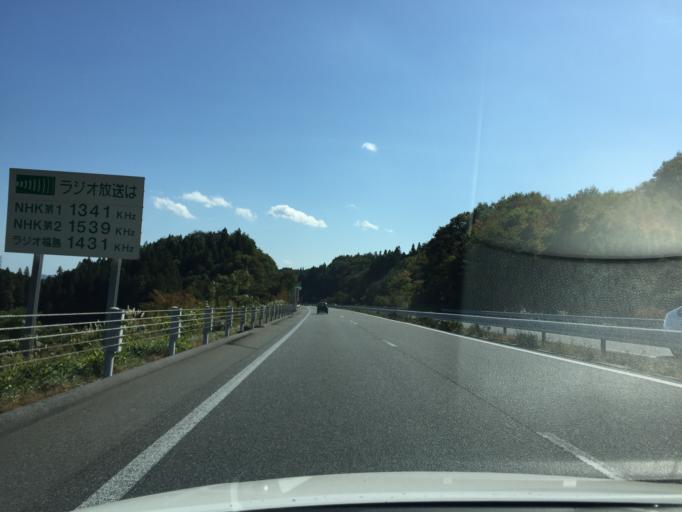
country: JP
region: Fukushima
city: Iwaki
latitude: 37.1883
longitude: 140.7088
